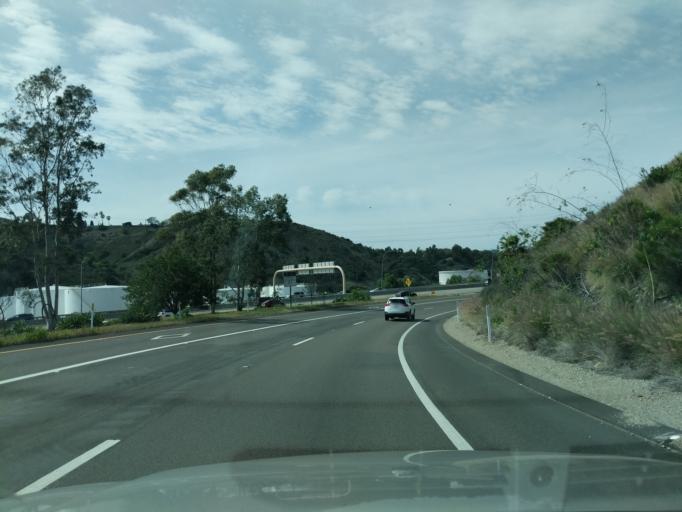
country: US
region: California
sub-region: San Diego County
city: San Diego
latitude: 32.7899
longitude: -117.1122
